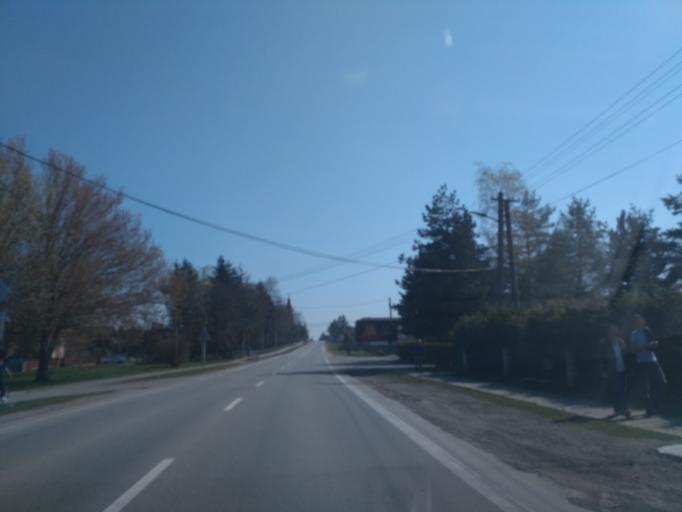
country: SK
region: Kosicky
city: Secovce
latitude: 48.7813
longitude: 21.6848
